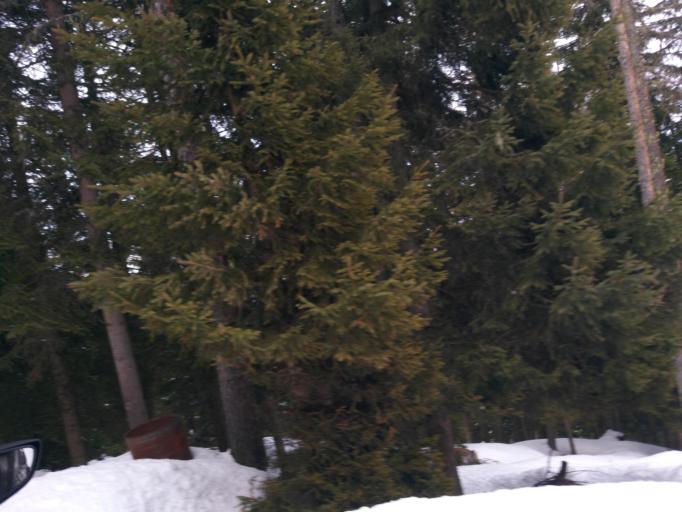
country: IT
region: Veneto
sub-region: Provincia di Belluno
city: Rocca Pietore
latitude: 46.4173
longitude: 11.9857
